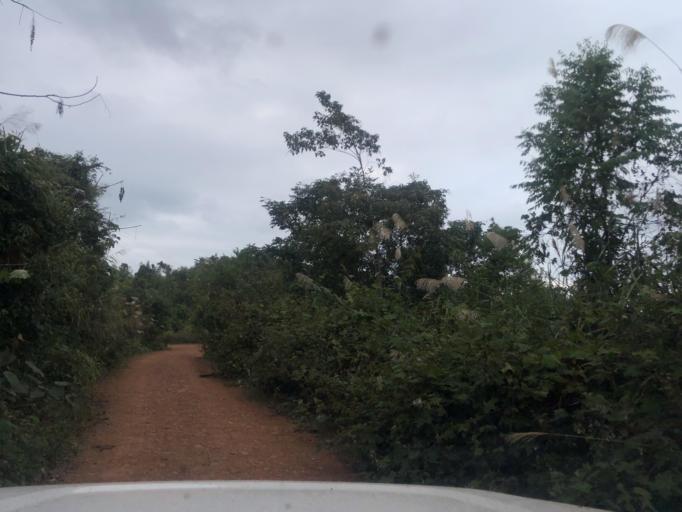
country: LA
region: Phongsali
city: Khoa
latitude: 21.2717
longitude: 102.5838
